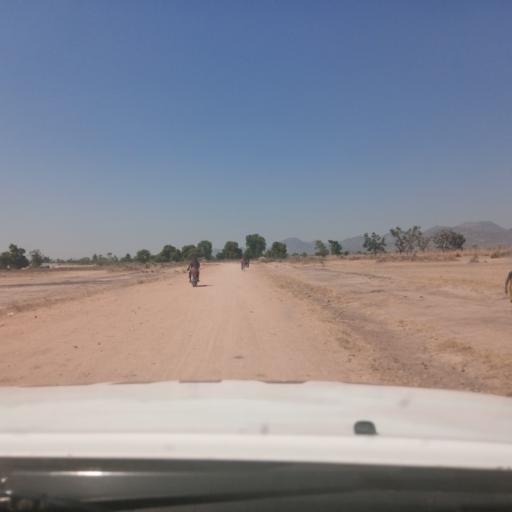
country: NG
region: Adamawa
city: Little Gombi
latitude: 9.7773
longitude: 12.5852
